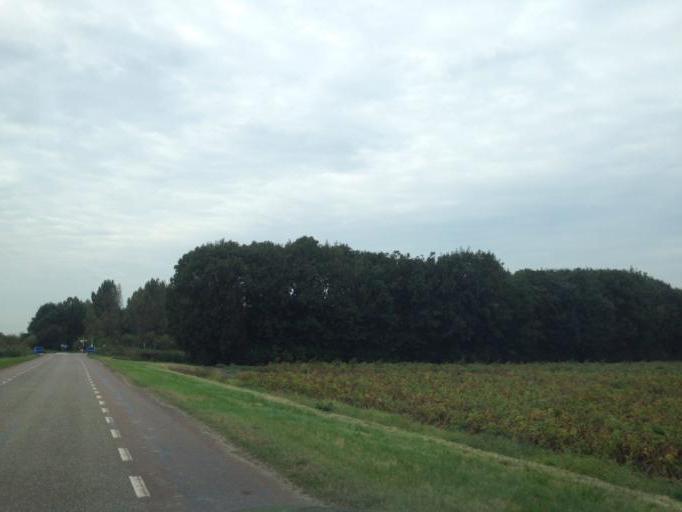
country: NL
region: Flevoland
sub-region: Gemeente Lelystad
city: Lelystad
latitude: 52.4177
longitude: 5.4074
